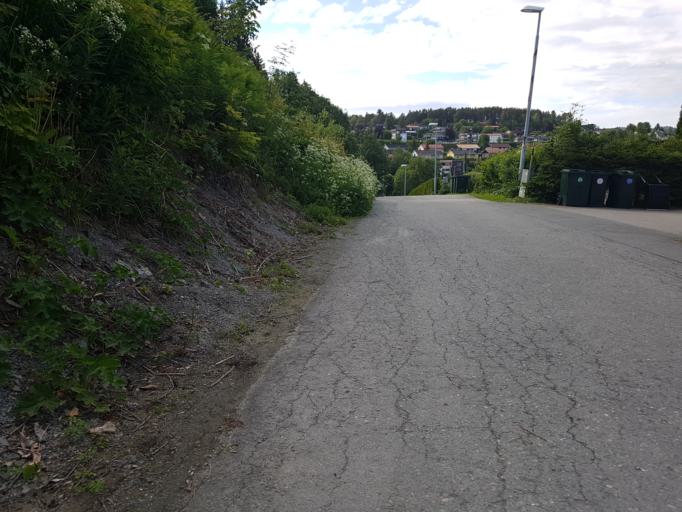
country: NO
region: Sor-Trondelag
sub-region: Trondheim
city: Trondheim
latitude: 63.4053
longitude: 10.3543
